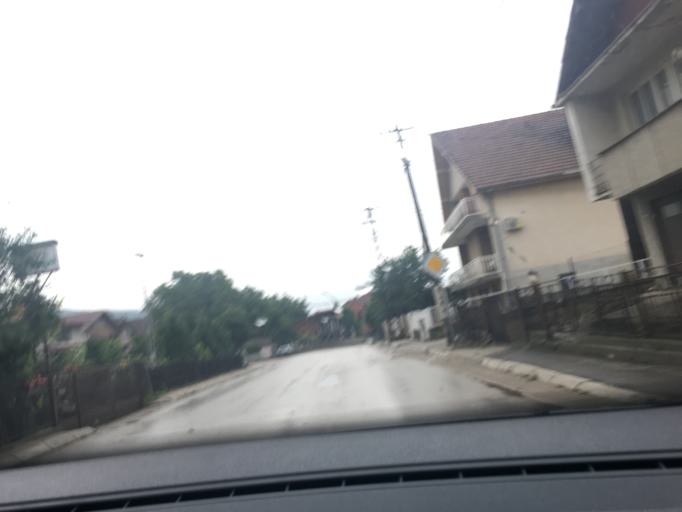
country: RS
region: Central Serbia
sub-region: Nisavski Okrug
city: Aleksinac
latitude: 43.5523
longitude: 21.7069
